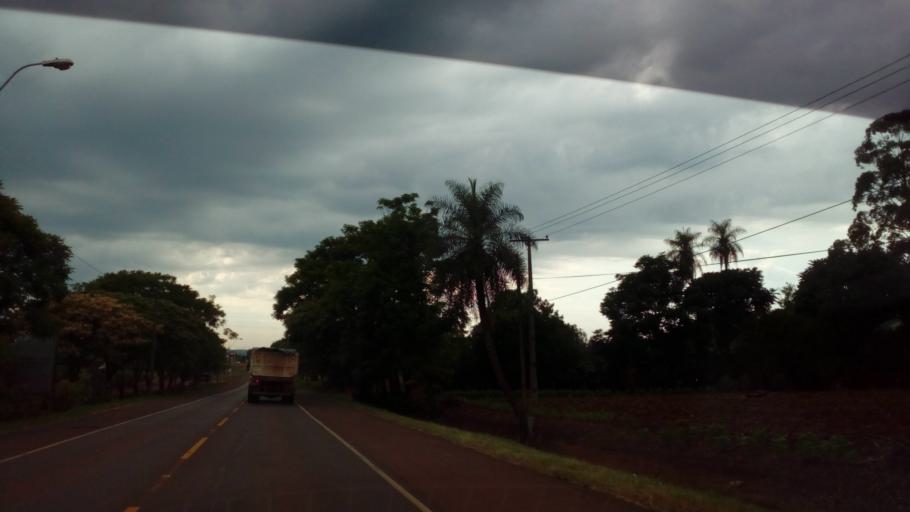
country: PY
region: Itapua
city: Obligado
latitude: -27.0726
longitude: -55.6280
